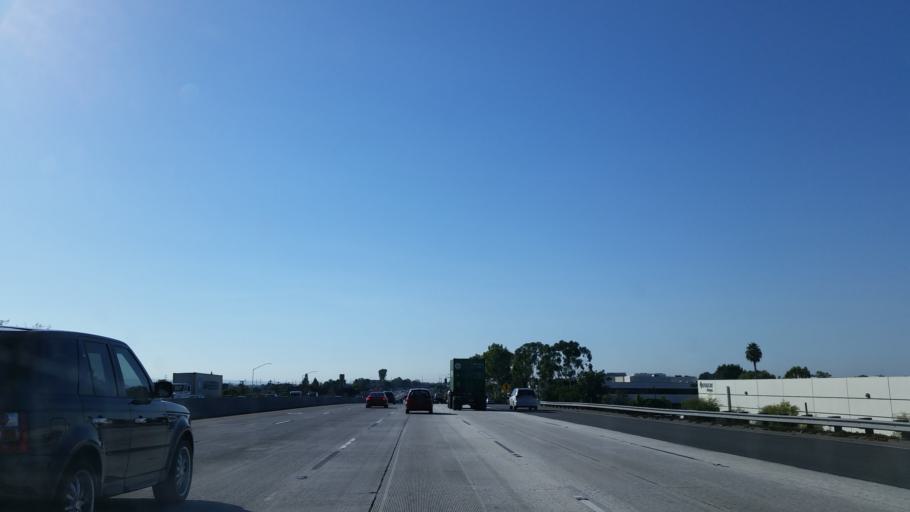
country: US
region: California
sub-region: Orange County
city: Buena Park
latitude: 33.8560
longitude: -118.0119
